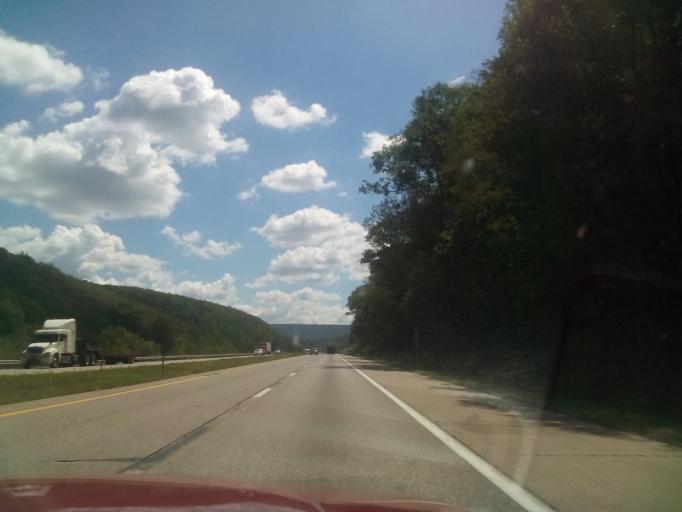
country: US
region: Pennsylvania
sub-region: Luzerne County
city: Nescopeck
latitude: 41.0147
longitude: -76.1682
